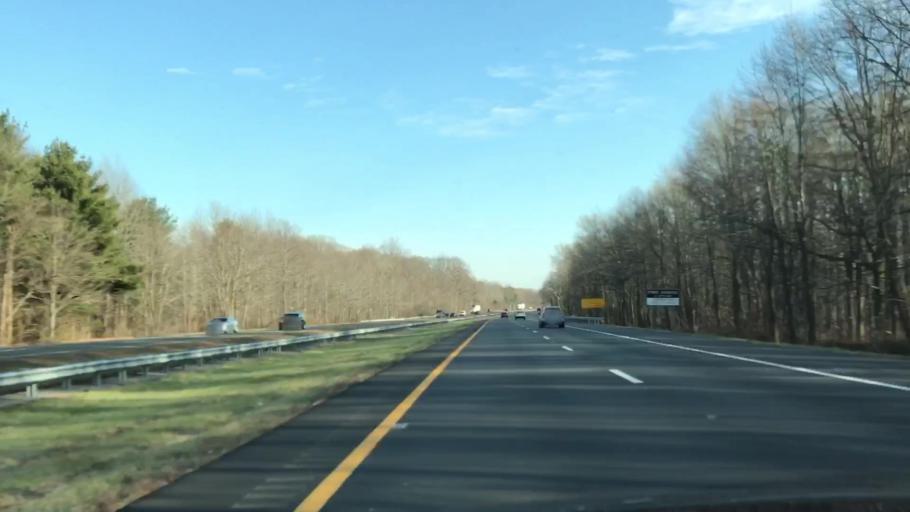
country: US
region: New Jersey
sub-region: Monmouth County
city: Allentown
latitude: 40.1905
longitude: -74.5860
